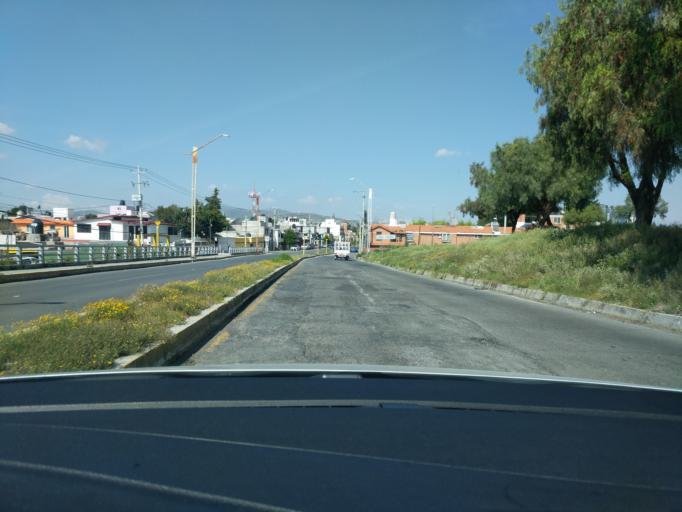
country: MX
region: Hidalgo
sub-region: Mineral de la Reforma
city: Rinconadas de San Francisco
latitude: 20.0875
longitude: -98.7661
